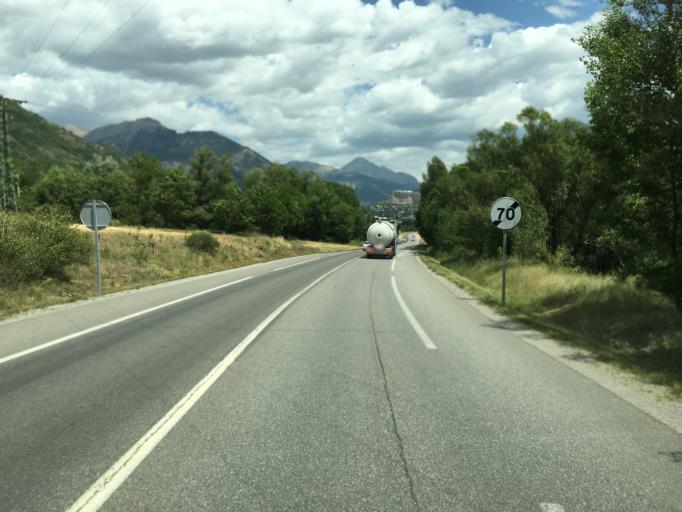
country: FR
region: Provence-Alpes-Cote d'Azur
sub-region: Departement des Hautes-Alpes
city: Villar-Saint-Pancrace
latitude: 44.8690
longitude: 6.6028
